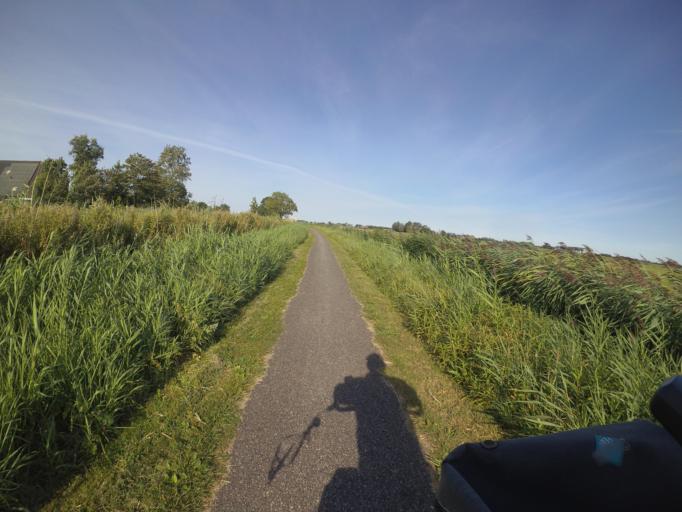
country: NL
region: Friesland
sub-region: Gemeente Dongeradeel
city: Dokkum
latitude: 53.3219
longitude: 5.9696
